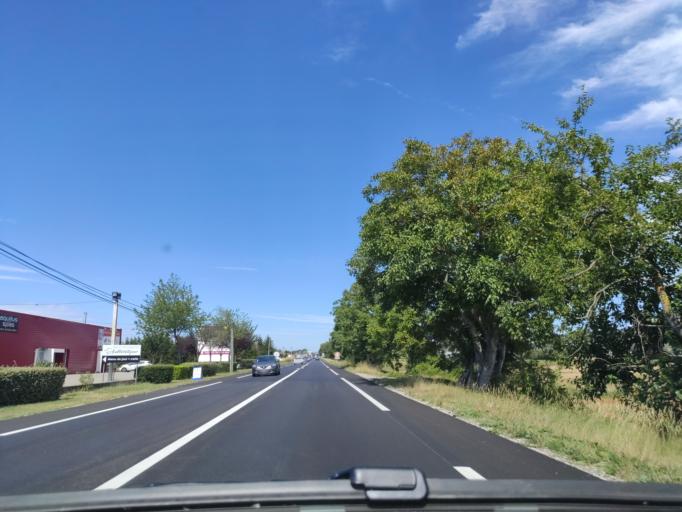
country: FR
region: Rhone-Alpes
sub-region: Departement de l'Isere
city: Reventin-Vaugris
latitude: 45.4526
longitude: 4.8236
